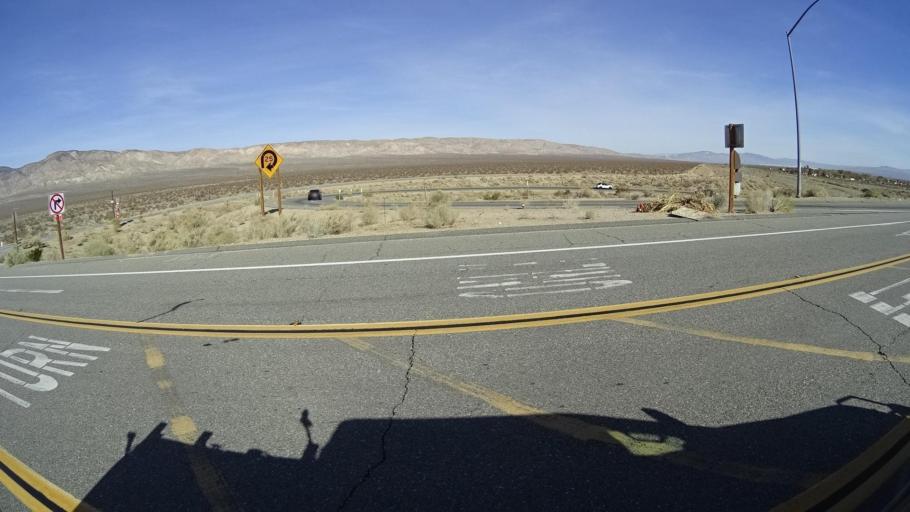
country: US
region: California
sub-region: Kern County
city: Mojave
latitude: 35.1251
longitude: -118.1251
